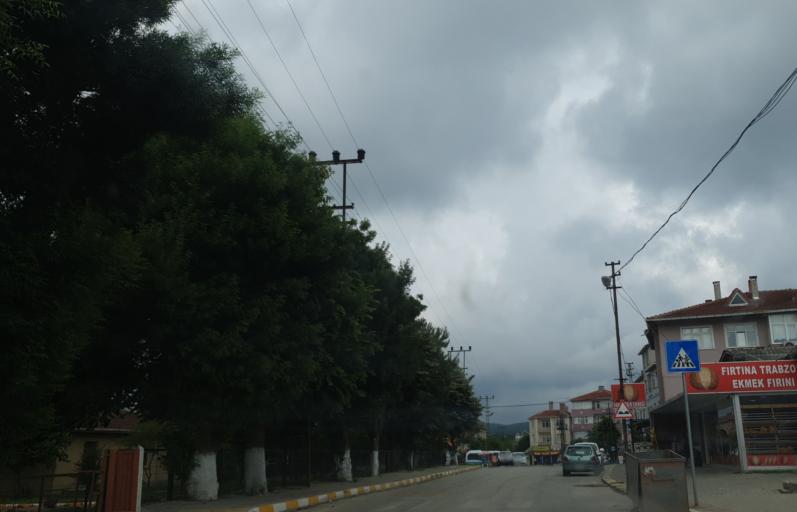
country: TR
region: Tekirdag
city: Saray
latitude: 41.4946
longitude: 27.9832
